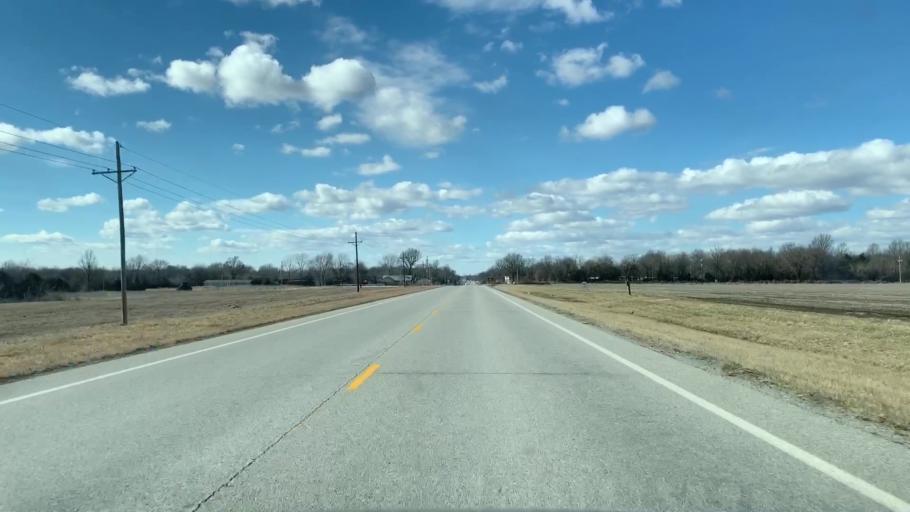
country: US
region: Kansas
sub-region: Cherokee County
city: Columbus
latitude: 37.1781
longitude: -94.8099
